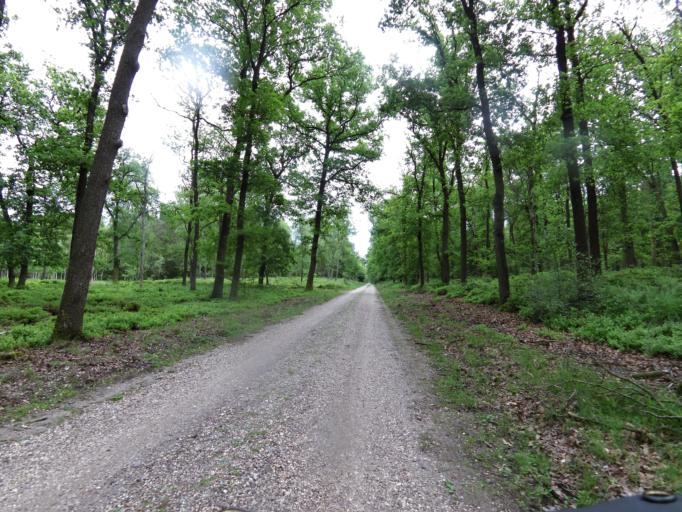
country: NL
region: Gelderland
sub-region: Gemeente Apeldoorn
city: Uddel
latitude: 52.2695
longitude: 5.8215
